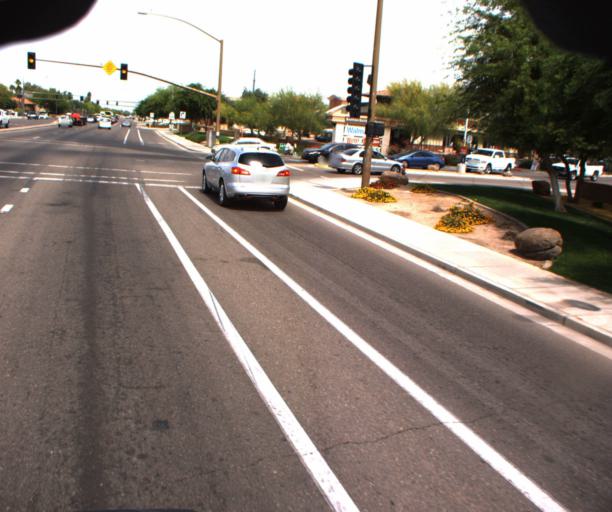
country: US
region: Arizona
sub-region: Maricopa County
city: Chandler
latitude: 33.2895
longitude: -111.8416
